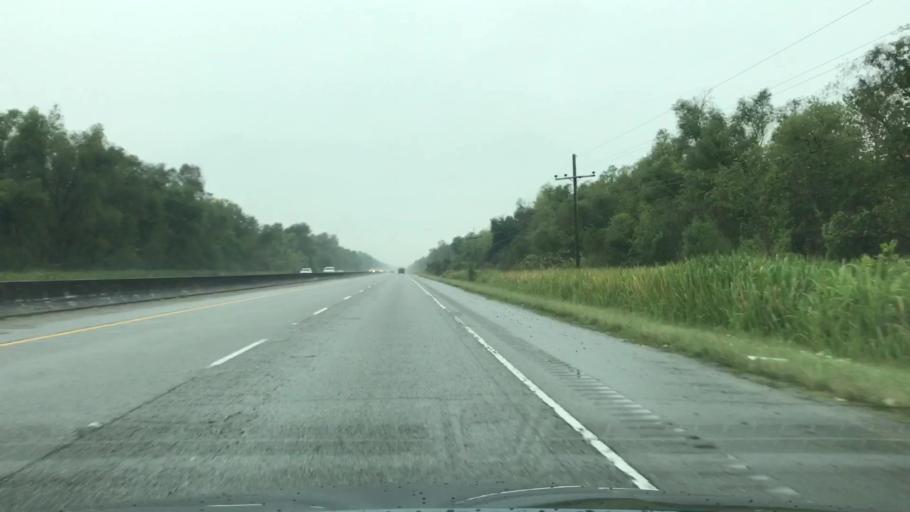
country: US
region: Louisiana
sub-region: Saint Charles Parish
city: Des Allemands
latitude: 29.7778
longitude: -90.5297
